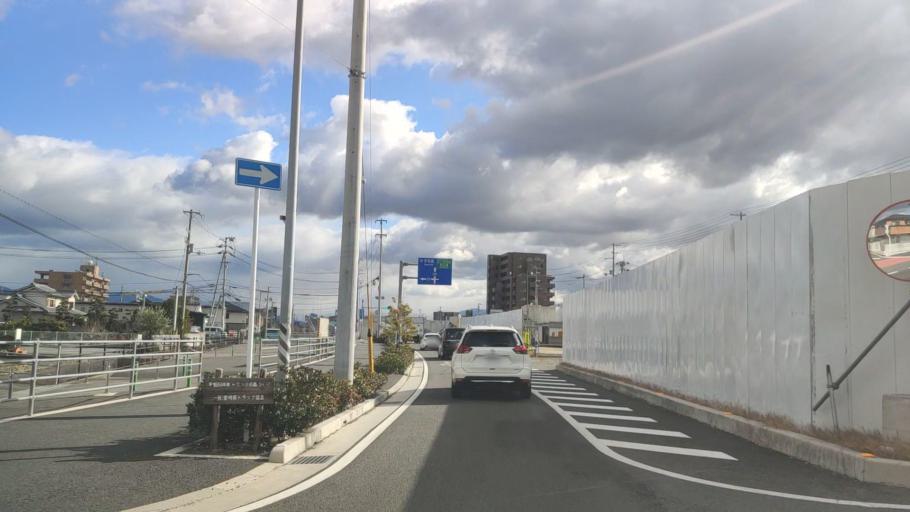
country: JP
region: Ehime
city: Masaki-cho
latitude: 33.8115
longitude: 132.7253
